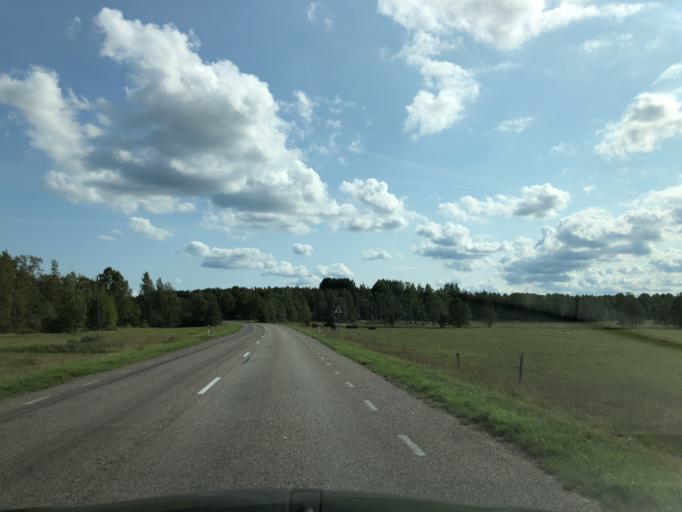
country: EE
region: Hiiumaa
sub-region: Kaerdla linn
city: Kardla
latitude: 58.7215
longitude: 22.5629
